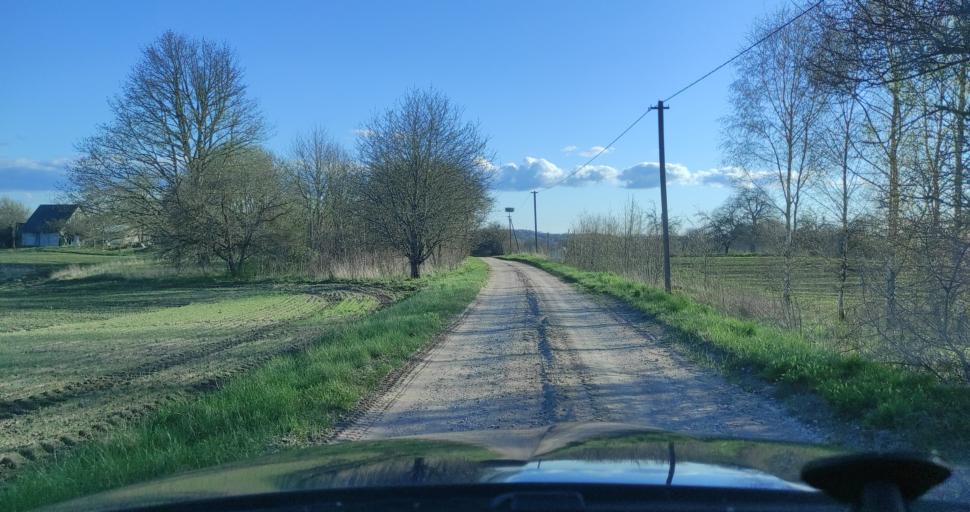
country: LV
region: Kuldigas Rajons
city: Kuldiga
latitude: 56.8785
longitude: 21.8357
